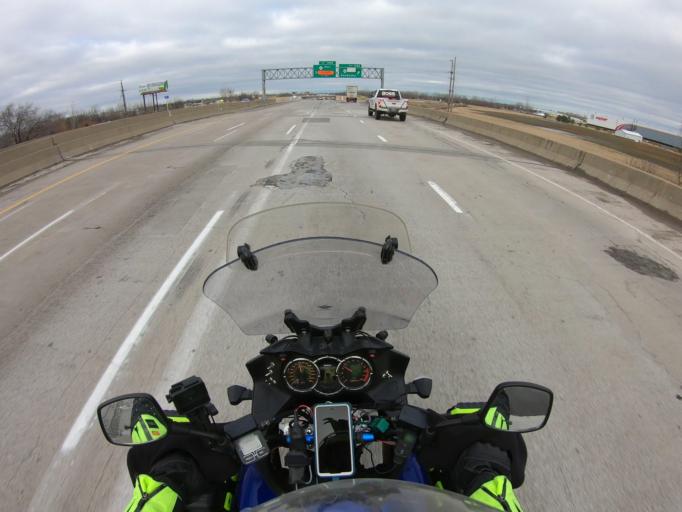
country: US
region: Michigan
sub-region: Saginaw County
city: Buena Vista
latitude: 43.4098
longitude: -83.8906
